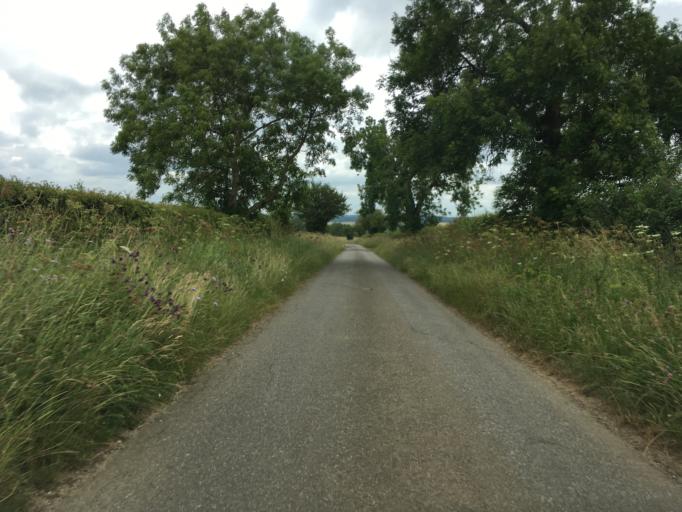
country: GB
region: England
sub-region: Oxfordshire
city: Charlbury
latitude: 51.9106
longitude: -1.5065
